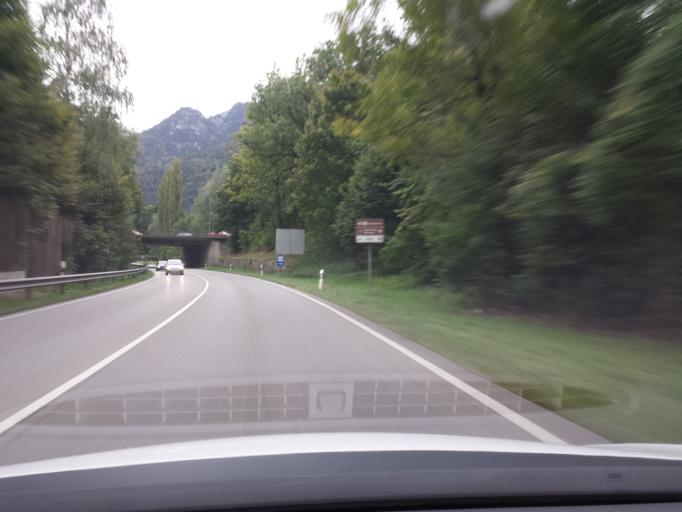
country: DE
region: Bavaria
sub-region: Upper Bavaria
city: Bad Reichenhall
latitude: 47.7236
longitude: 12.8673
